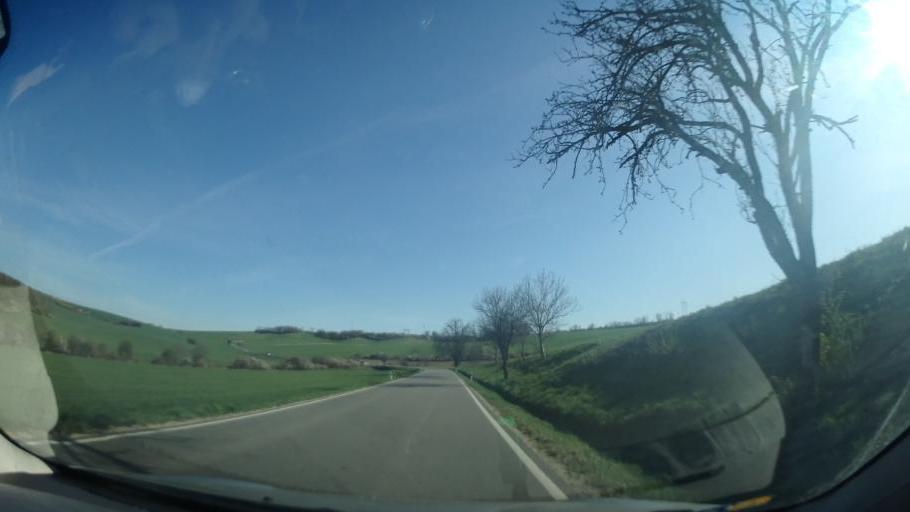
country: CZ
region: South Moravian
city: Ostopovice
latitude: 49.1570
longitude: 16.5524
